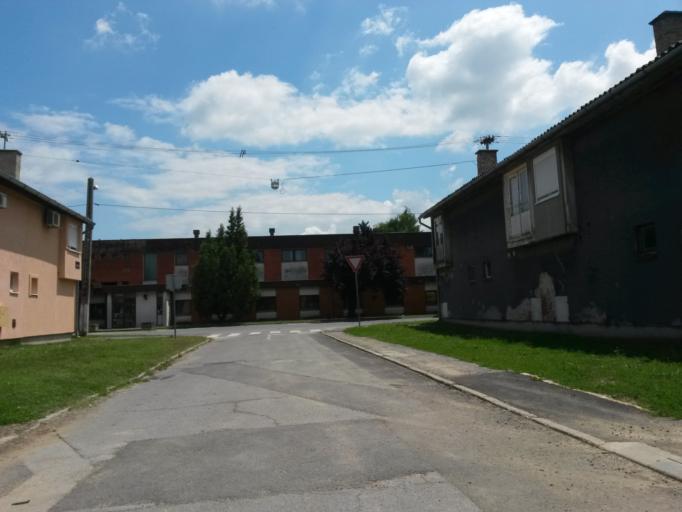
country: HR
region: Osjecko-Baranjska
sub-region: Grad Osijek
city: Osijek
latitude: 45.5542
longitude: 18.7309
